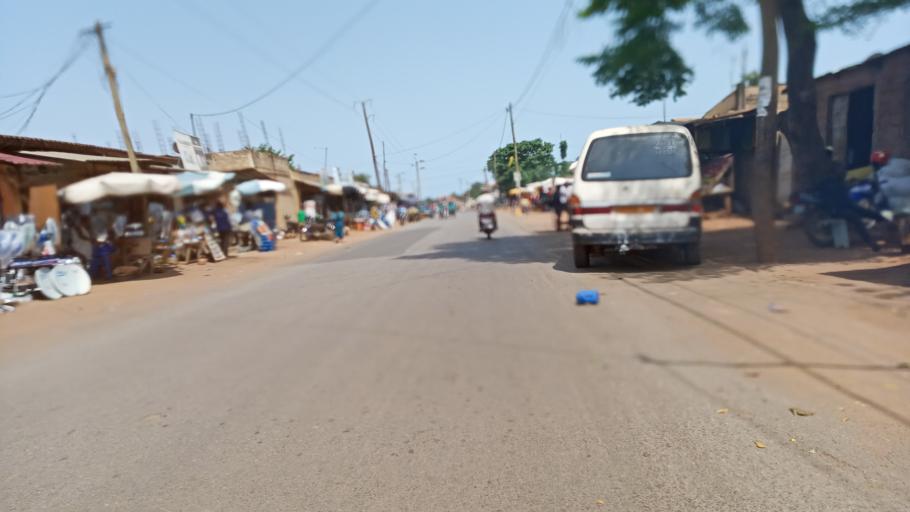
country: TG
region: Maritime
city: Lome
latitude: 6.2249
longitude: 1.2059
